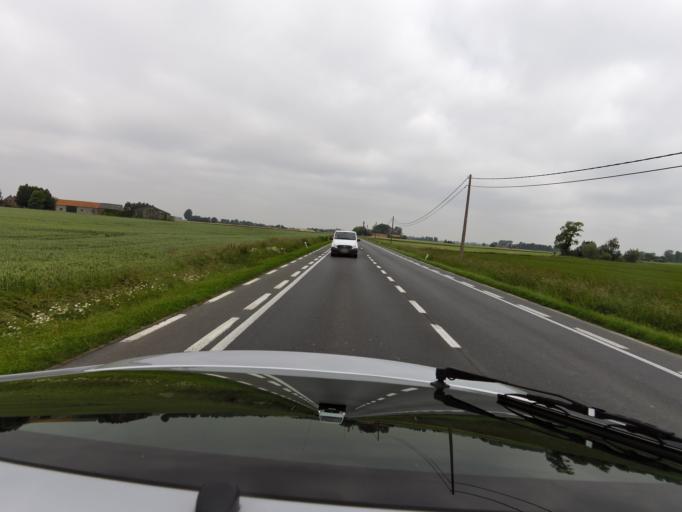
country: BE
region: Flanders
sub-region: Provincie West-Vlaanderen
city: Alveringem
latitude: 51.0092
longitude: 2.6830
